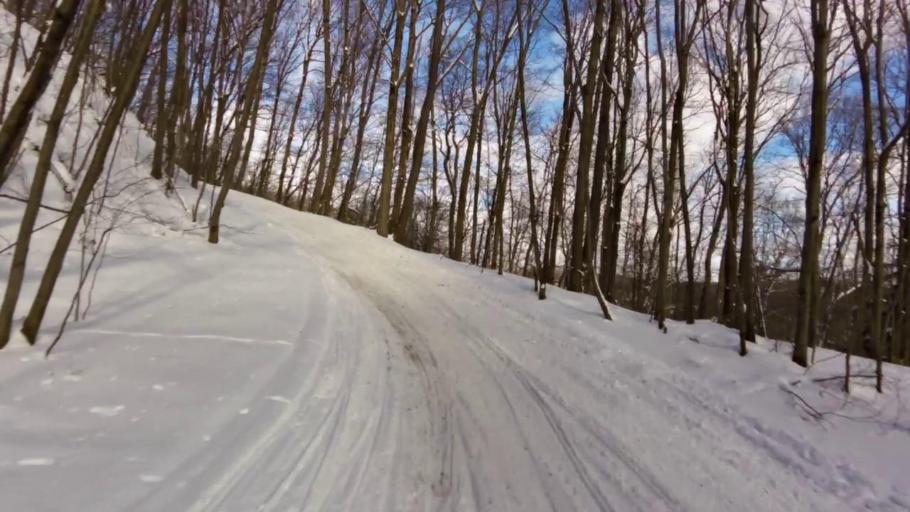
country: US
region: New York
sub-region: Cattaraugus County
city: Salamanca
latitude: 42.0617
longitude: -78.6955
